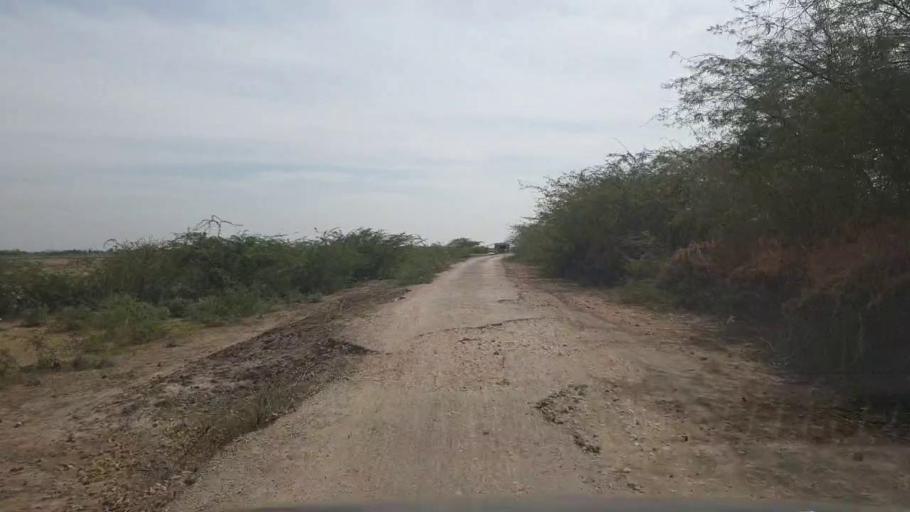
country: PK
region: Sindh
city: Kunri
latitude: 25.2683
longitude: 69.6021
